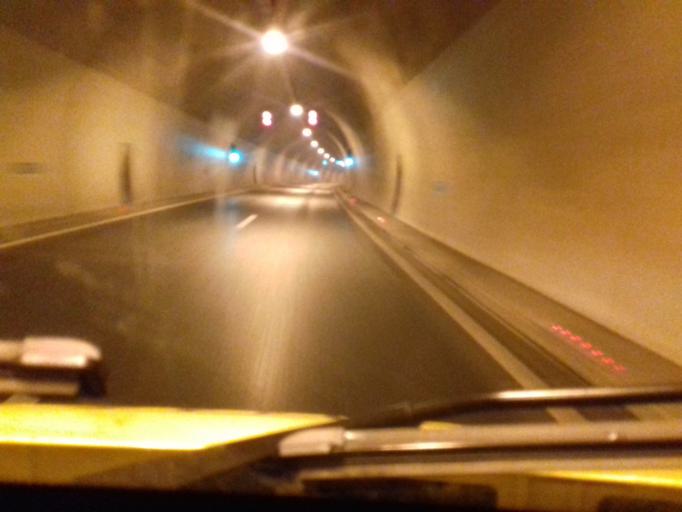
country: BA
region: Federation of Bosnia and Herzegovina
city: Vogosca
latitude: 43.8903
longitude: 18.3160
